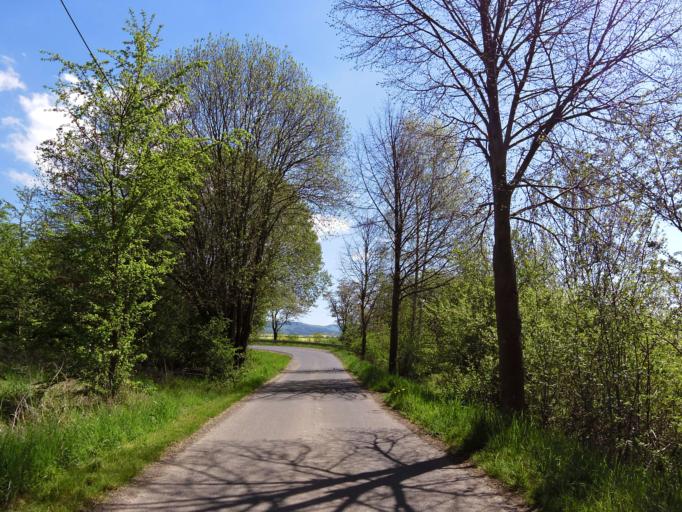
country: DE
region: Thuringia
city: Bad Salzungen
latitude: 50.8686
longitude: 10.2292
